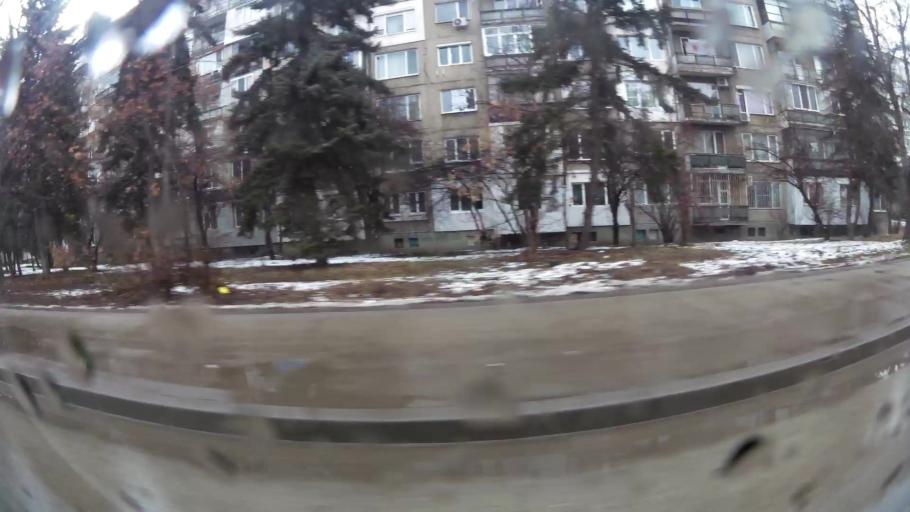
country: BG
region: Sofia-Capital
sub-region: Stolichna Obshtina
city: Sofia
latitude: 42.6664
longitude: 23.2850
